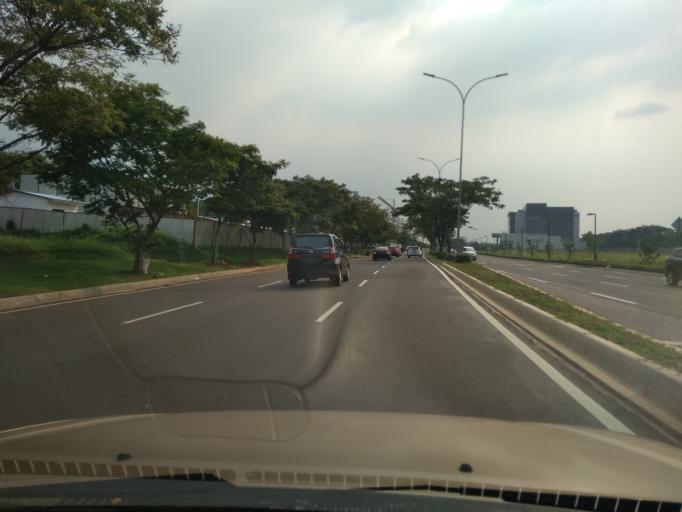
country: ID
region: West Java
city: Serpong
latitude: -6.2893
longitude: 106.6489
